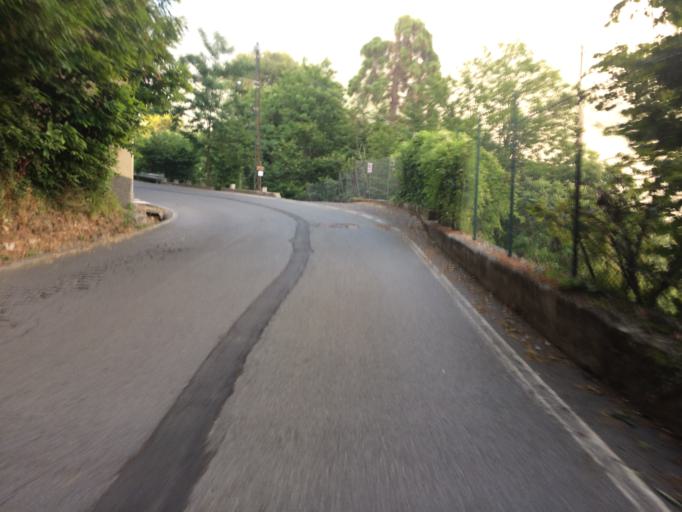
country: IT
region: Liguria
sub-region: Provincia di Imperia
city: Seborga
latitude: 43.8571
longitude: 7.7285
